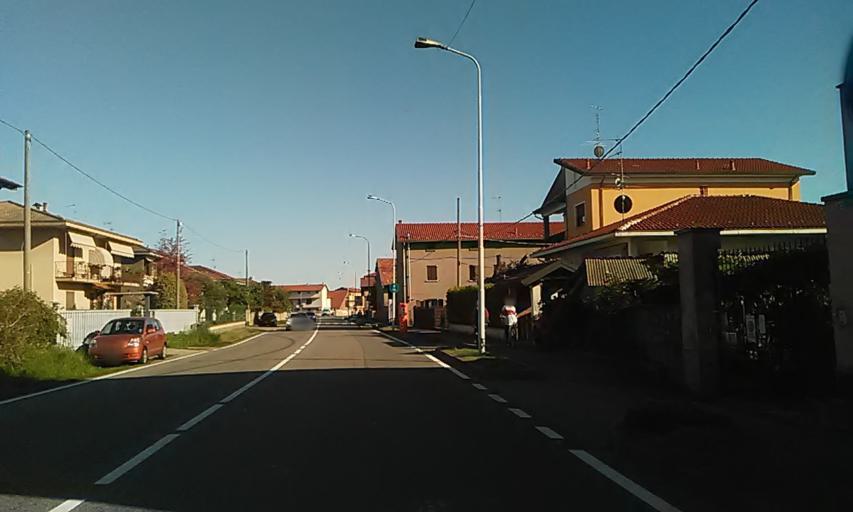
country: IT
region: Piedmont
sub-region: Provincia di Novara
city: Momo
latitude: 45.5795
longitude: 8.5523
